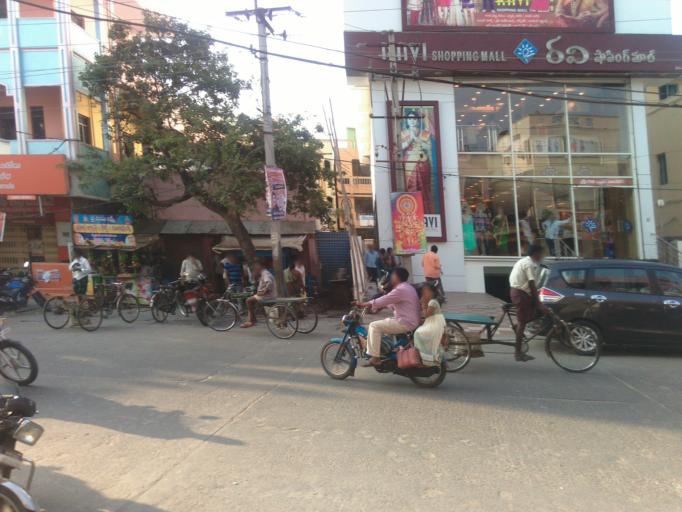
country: IN
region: Andhra Pradesh
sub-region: Prakasam
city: Chirala
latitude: 15.8264
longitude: 80.3544
